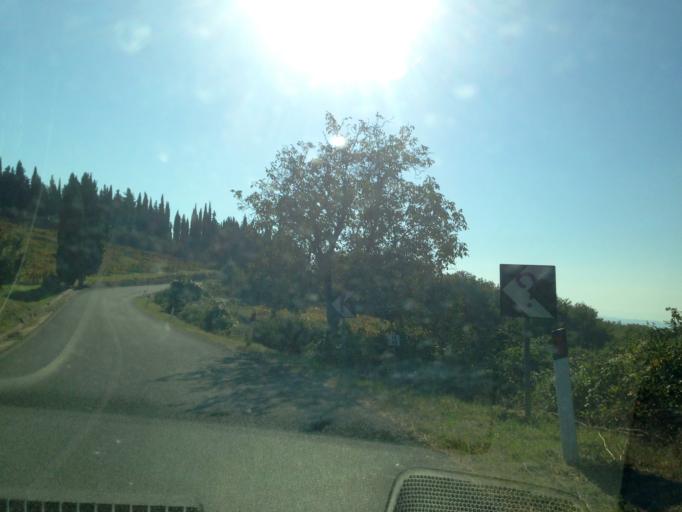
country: IT
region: Tuscany
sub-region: Provincia di Siena
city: Castellina in Chianti
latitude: 43.4502
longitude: 11.2932
